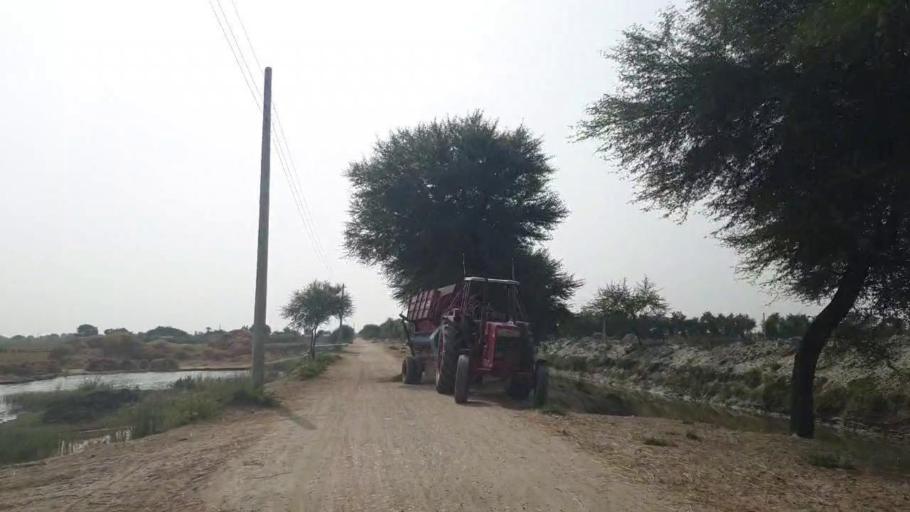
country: PK
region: Sindh
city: Badin
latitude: 24.6163
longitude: 68.7228
